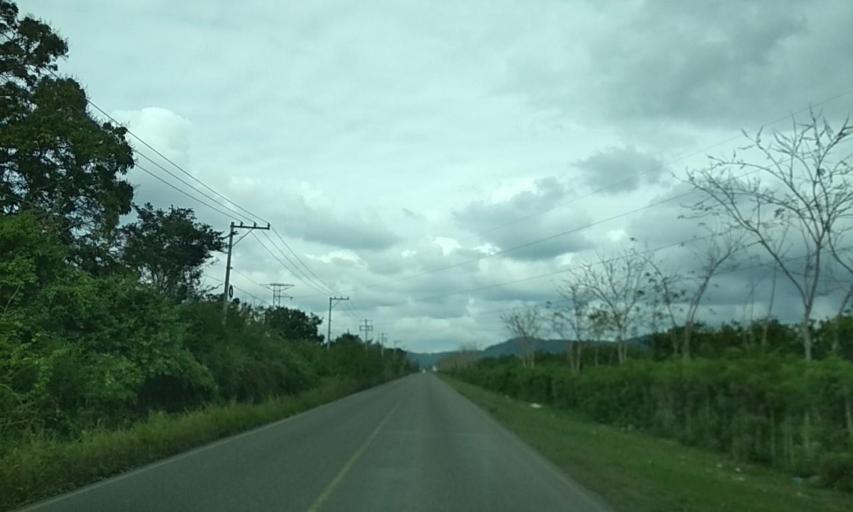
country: MX
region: Veracruz
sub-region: Papantla
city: El Chote
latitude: 20.3844
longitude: -97.3367
